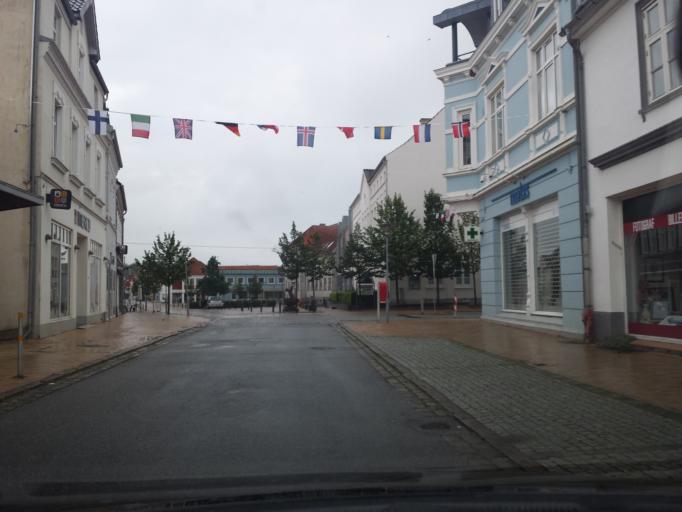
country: DK
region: South Denmark
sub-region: Sonderborg Kommune
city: Grasten
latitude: 54.9214
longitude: 9.5928
